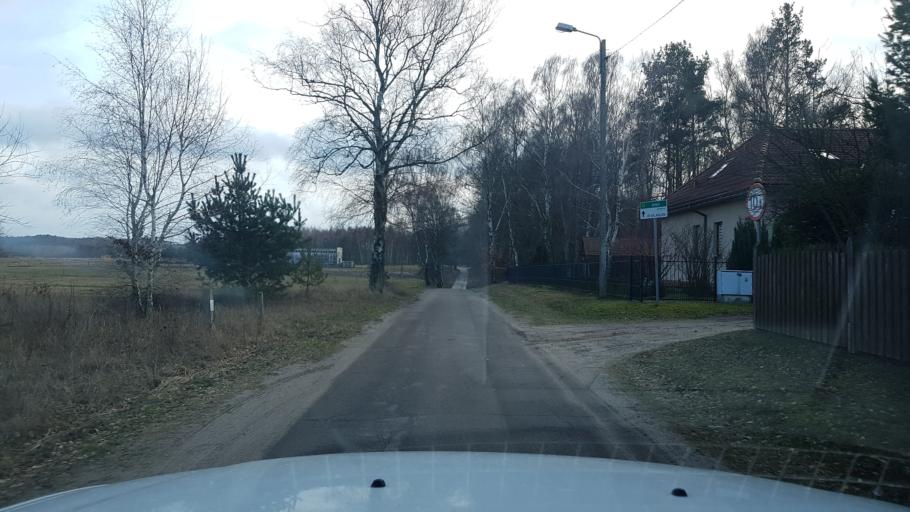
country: PL
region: West Pomeranian Voivodeship
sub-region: Powiat szczecinecki
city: Borne Sulinowo
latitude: 53.6293
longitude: 16.6125
